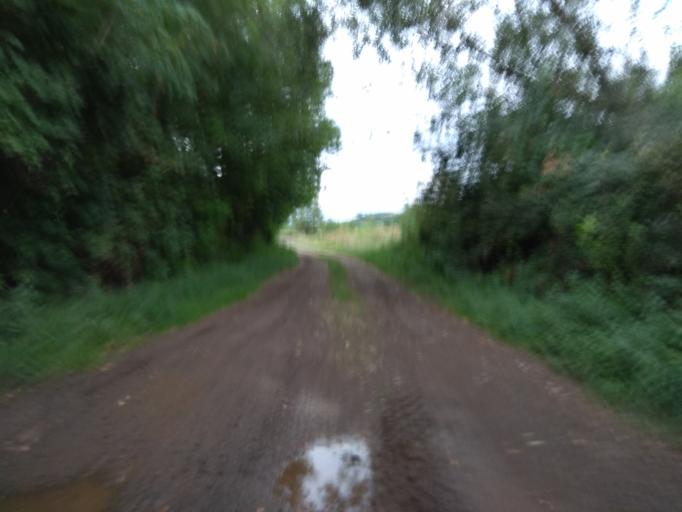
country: HU
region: Borsod-Abauj-Zemplen
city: Monok
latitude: 48.1736
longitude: 21.1200
